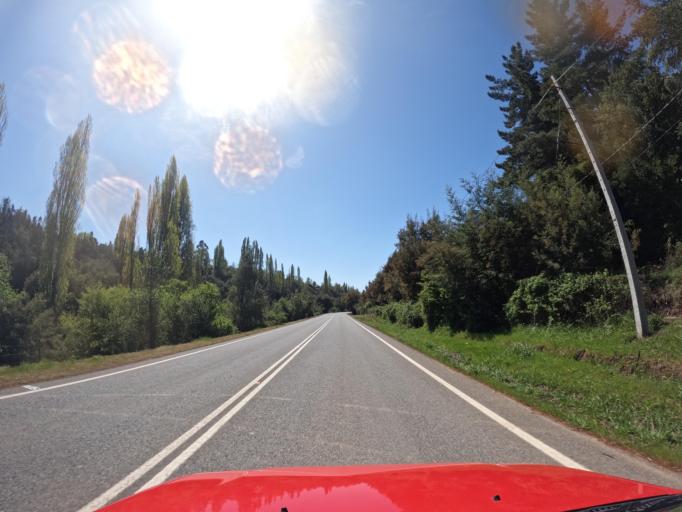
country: CL
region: Maule
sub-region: Provincia de Talca
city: San Clemente
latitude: -35.4599
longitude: -71.2697
